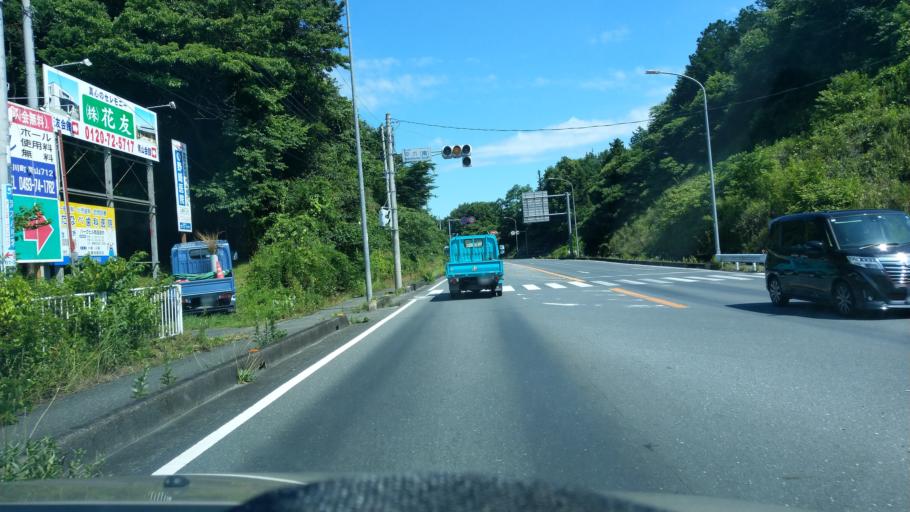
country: JP
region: Saitama
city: Ogawa
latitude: 36.0637
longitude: 139.2897
